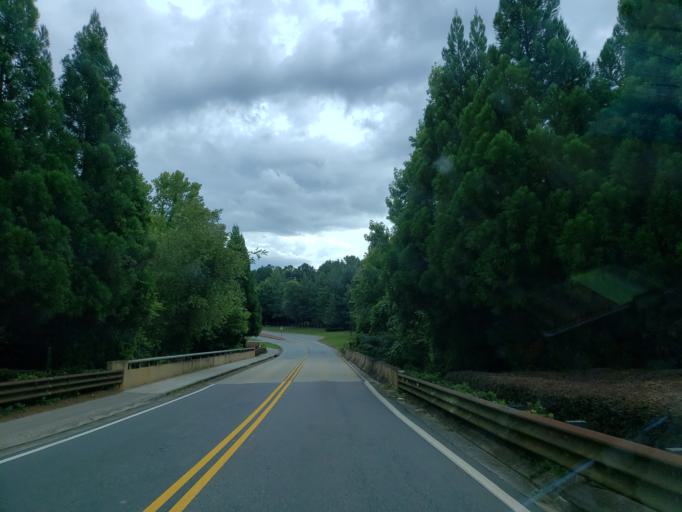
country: US
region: Georgia
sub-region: Bartow County
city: Emerson
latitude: 34.0215
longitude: -84.7846
